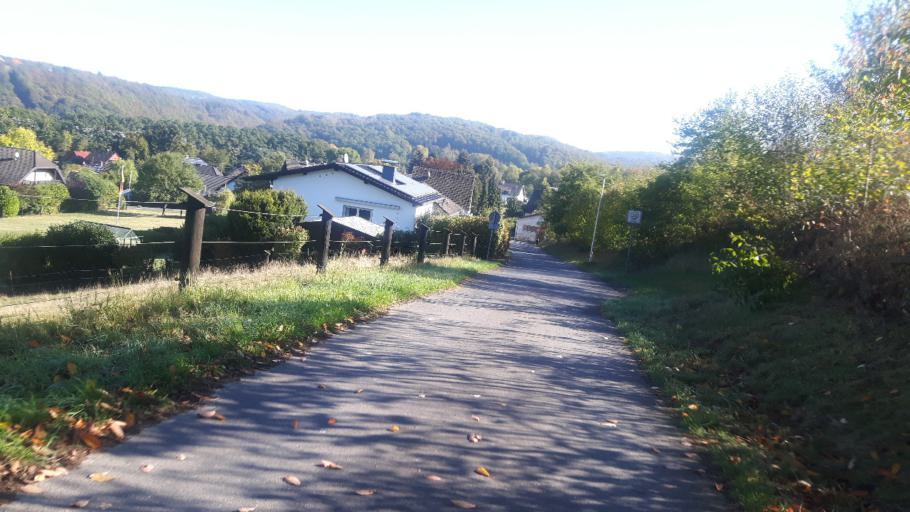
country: DE
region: Rheinland-Pfalz
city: Niederirsen
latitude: 50.8028
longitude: 7.5989
